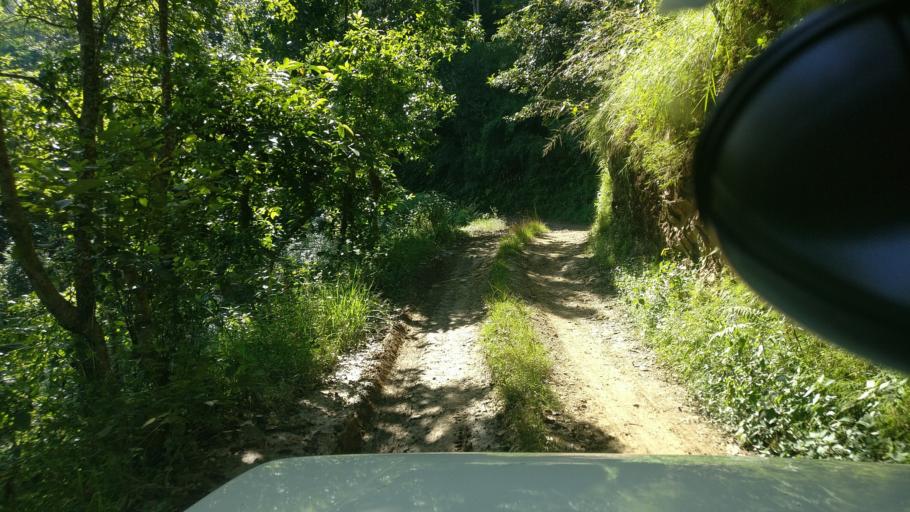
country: NP
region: Western Region
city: Baglung
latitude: 28.1319
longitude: 83.6606
